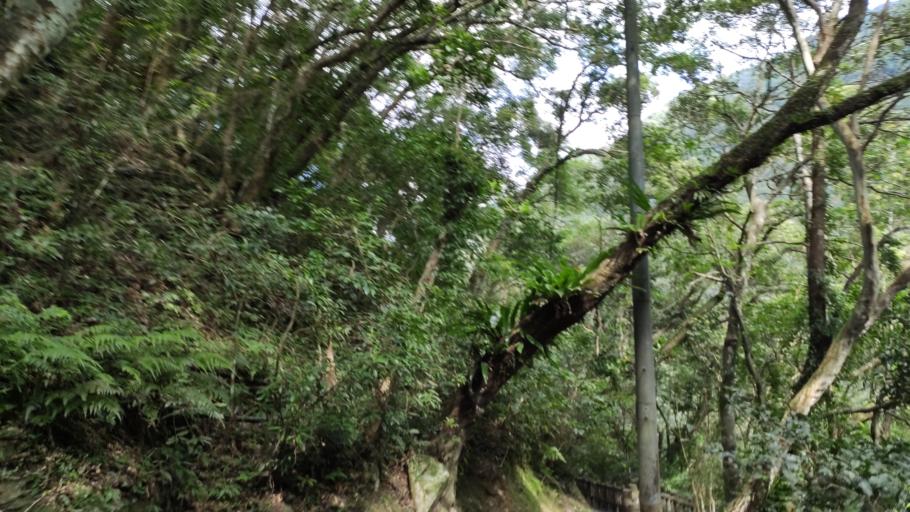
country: TW
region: Taiwan
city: Daxi
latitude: 24.8187
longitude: 121.4497
